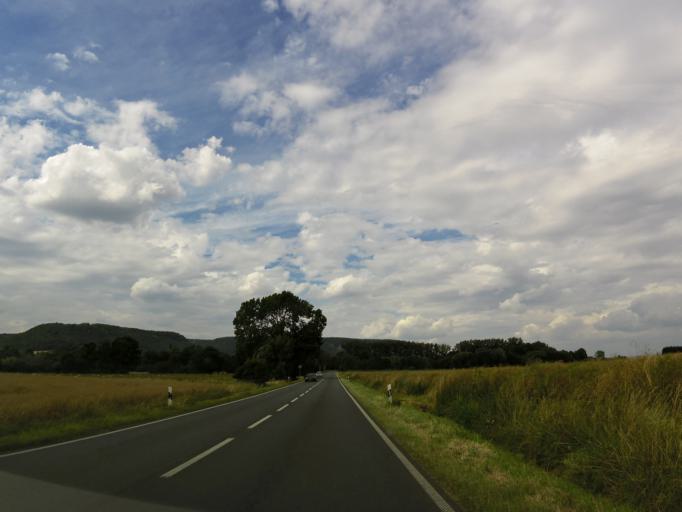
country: DE
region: Lower Saxony
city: Boffzen
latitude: 51.7249
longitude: 9.3711
